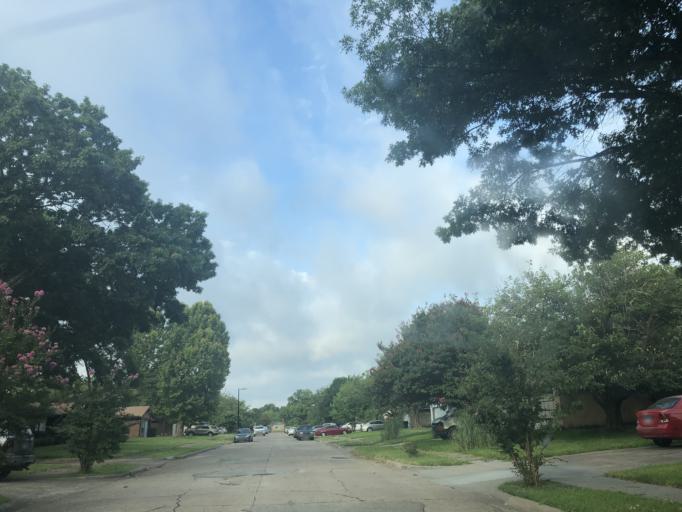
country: US
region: Texas
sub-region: Dallas County
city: Garland
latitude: 32.8501
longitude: -96.6248
